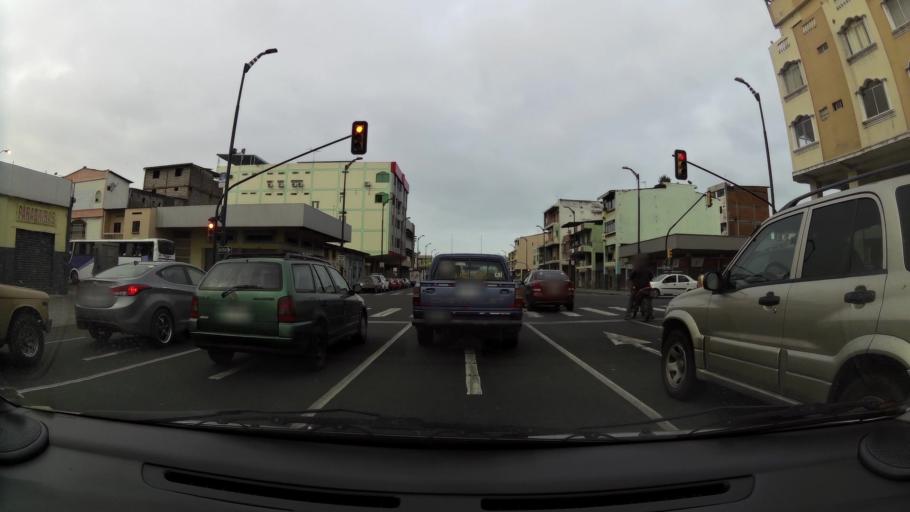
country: EC
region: Guayas
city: Guayaquil
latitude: -2.1996
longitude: -79.8931
